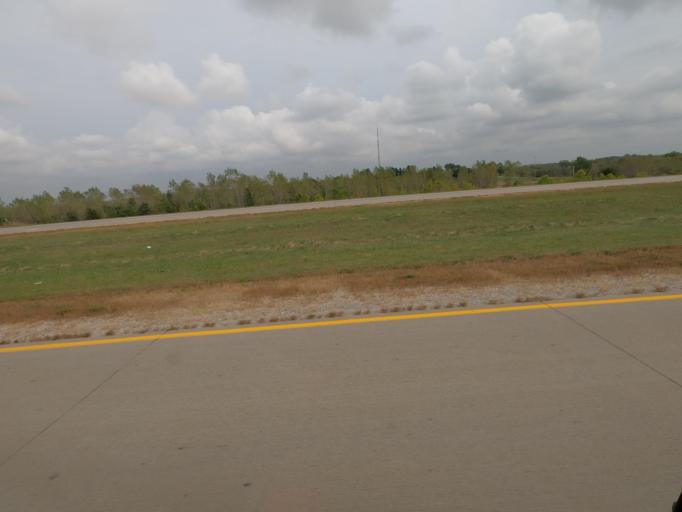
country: US
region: Iowa
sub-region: Wapello County
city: Ottumwa
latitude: 41.0777
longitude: -92.3940
